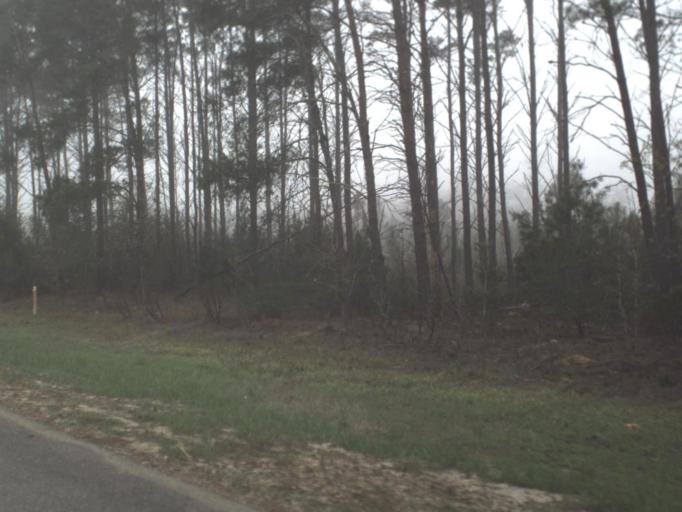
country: US
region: Florida
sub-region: Gadsden County
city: Gretna
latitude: 30.4820
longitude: -84.7251
